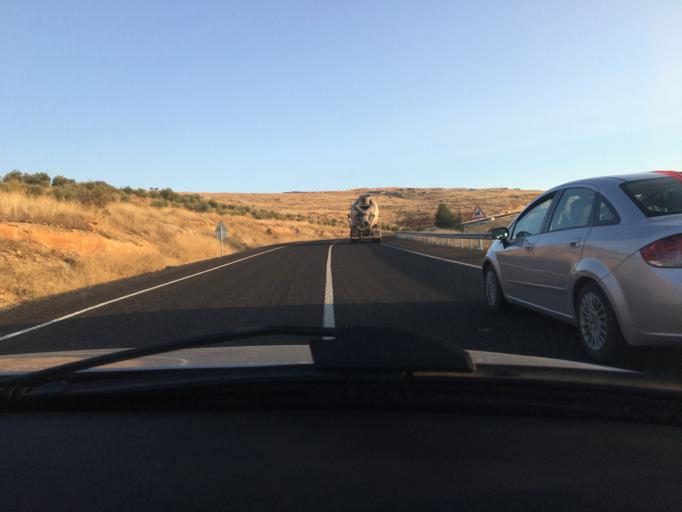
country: TR
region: Sanliurfa
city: Bogurtlen
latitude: 37.1866
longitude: 37.9746
